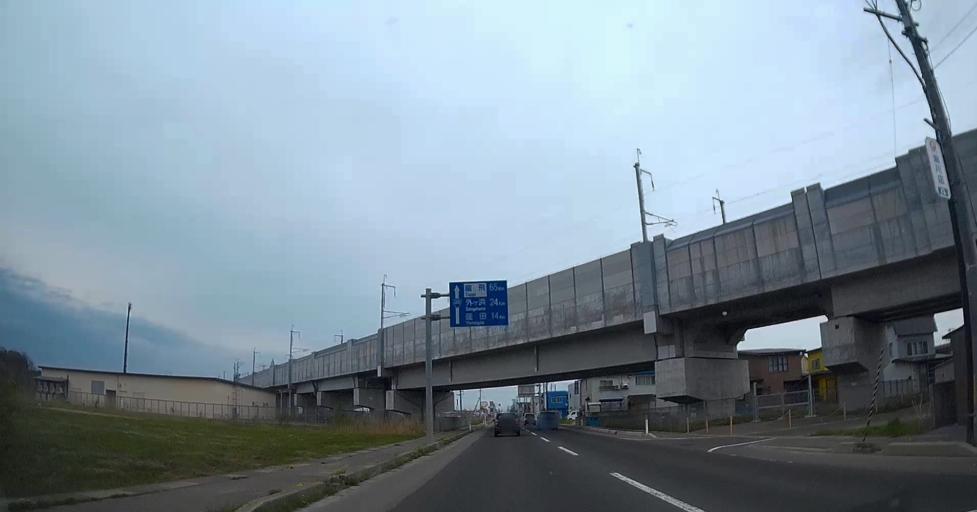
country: JP
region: Aomori
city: Aomori Shi
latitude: 40.8529
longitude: 140.6814
